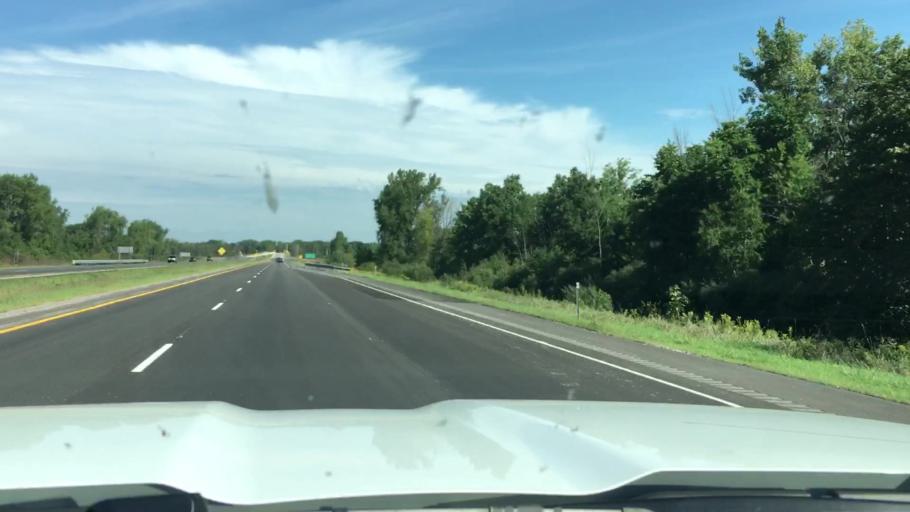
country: US
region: Michigan
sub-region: Saginaw County
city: Freeland
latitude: 43.5886
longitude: -84.1393
